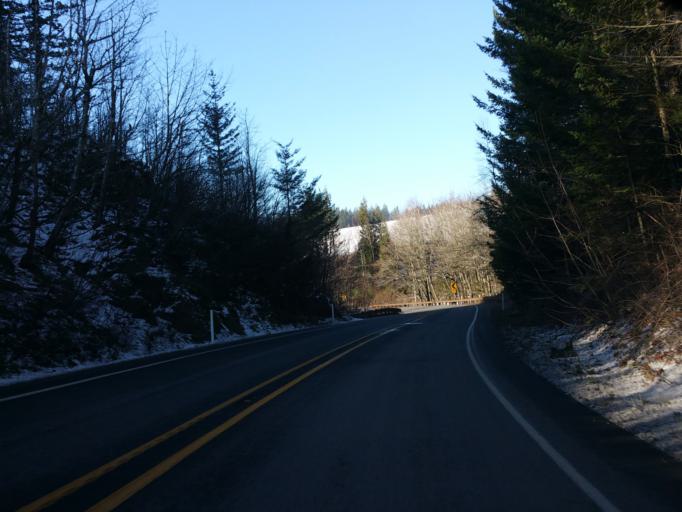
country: US
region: Washington
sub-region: Clark County
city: Washougal
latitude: 45.5659
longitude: -122.2165
